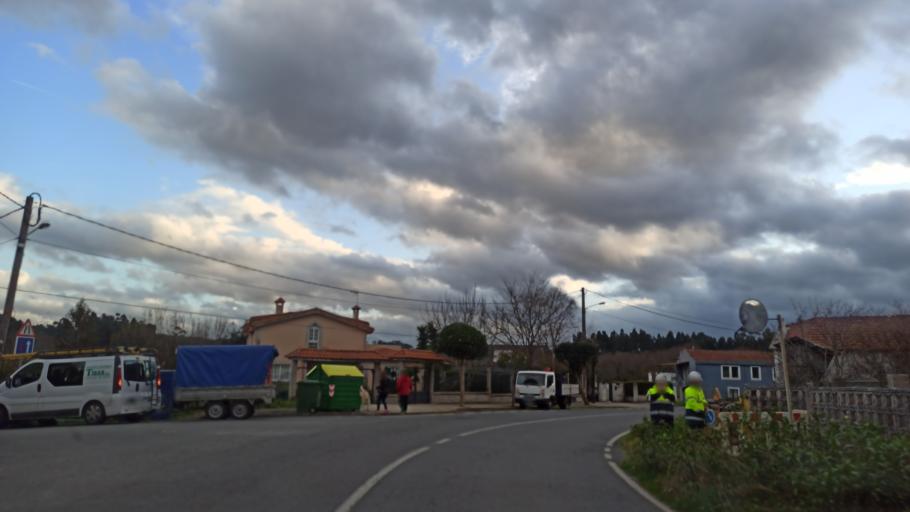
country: ES
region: Galicia
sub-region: Provincia da Coruna
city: Oleiros
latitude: 43.3830
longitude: -8.3226
